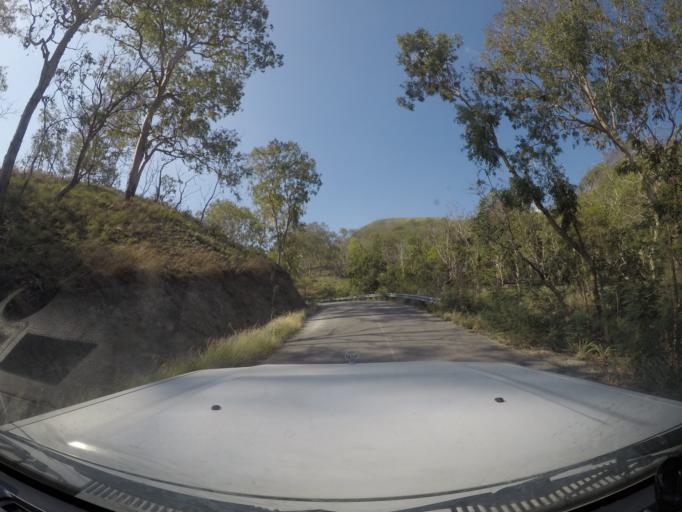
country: PG
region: Central Province
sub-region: Rigo
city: Kwikila
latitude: -9.8694
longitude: 147.5647
